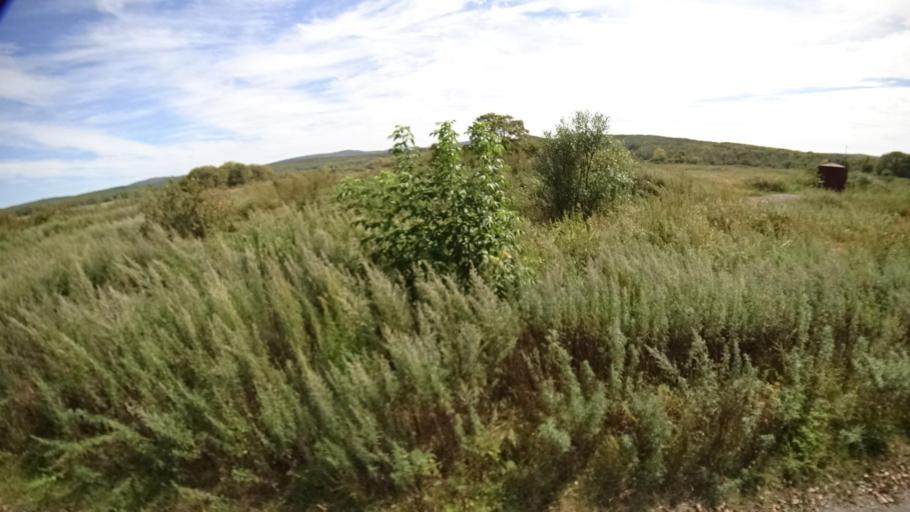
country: RU
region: Primorskiy
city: Yakovlevka
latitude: 44.6404
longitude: 133.6017
